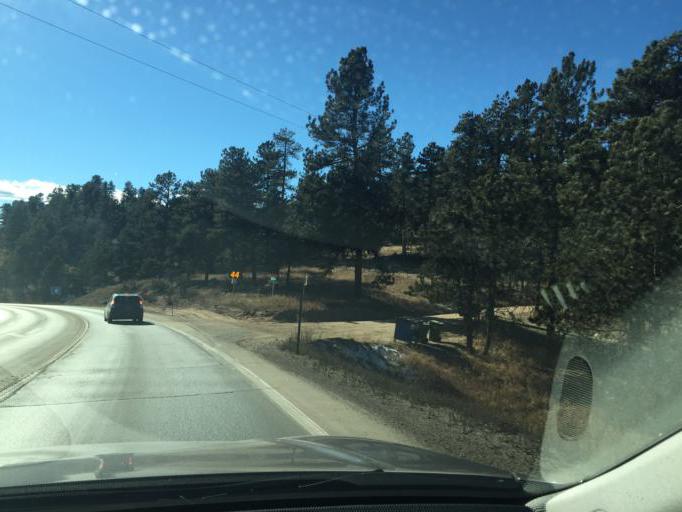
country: US
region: Colorado
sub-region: Jefferson County
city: Evergreen
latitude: 39.4838
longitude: -105.3640
